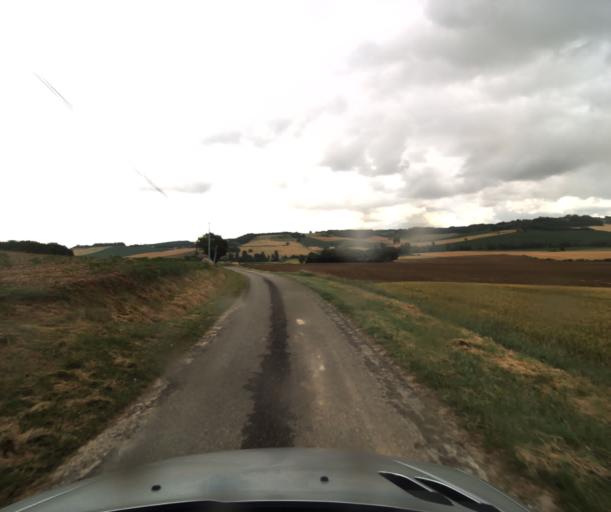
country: FR
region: Midi-Pyrenees
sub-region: Departement du Tarn-et-Garonne
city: Lavit
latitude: 43.9525
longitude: 0.9288
